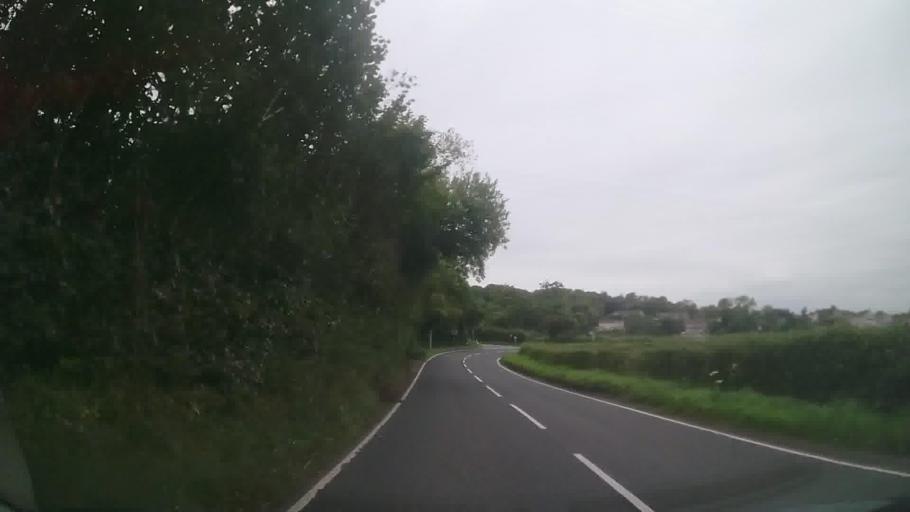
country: GB
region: Wales
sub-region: Carmarthenshire
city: Saint Clears
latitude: 51.8076
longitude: -4.4983
